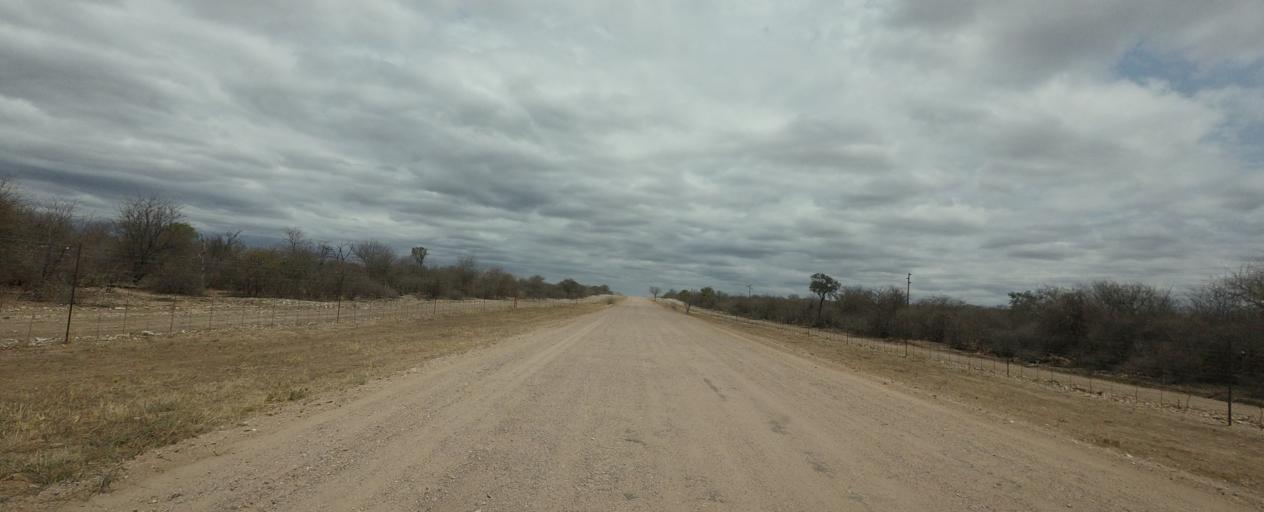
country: BW
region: Central
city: Mathathane
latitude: -22.6901
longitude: 28.6393
